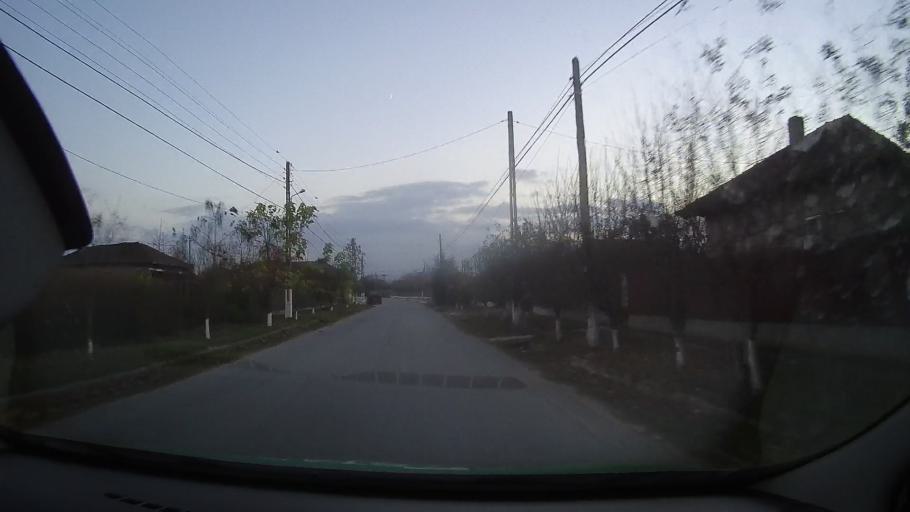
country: RO
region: Constanta
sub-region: Comuna Oltina
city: Oltina
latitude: 44.1679
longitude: 27.6651
